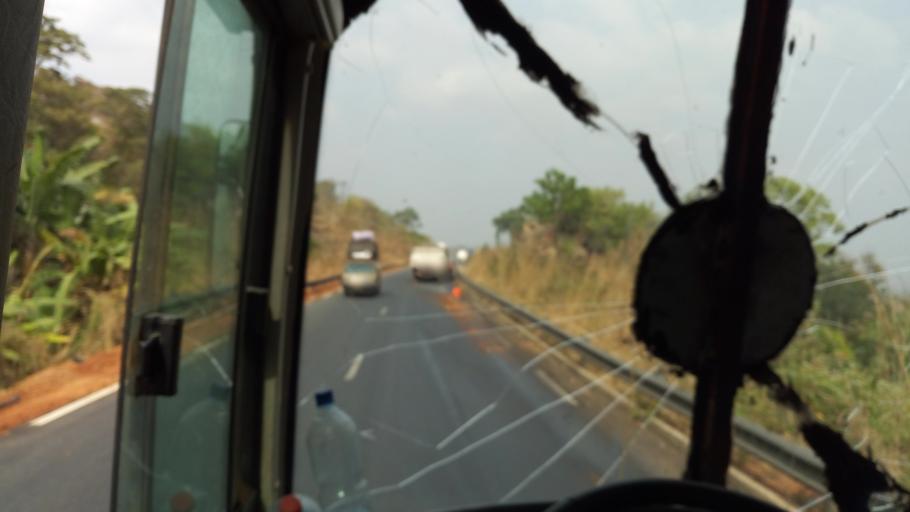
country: TG
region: Kara
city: Bafilo
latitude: 9.2418
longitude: 1.2119
